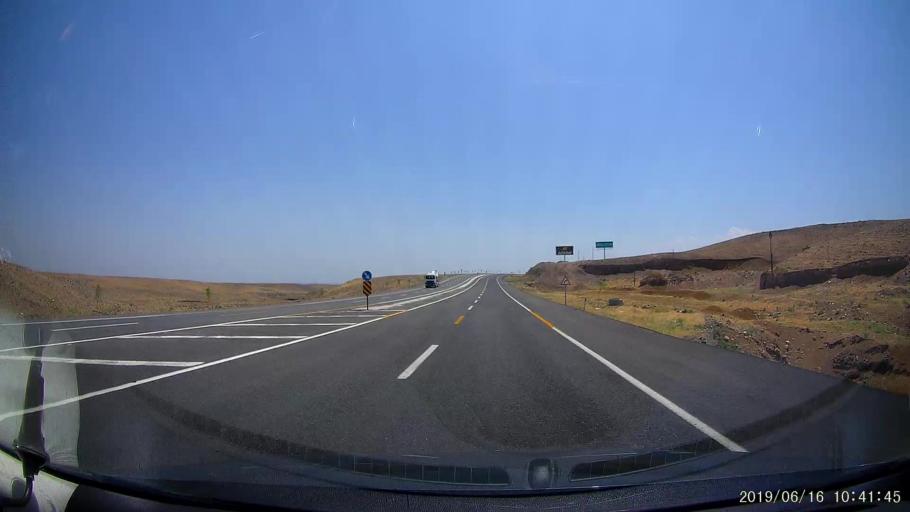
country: AM
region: Armavir
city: Shenavan
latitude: 40.0462
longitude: 43.7909
